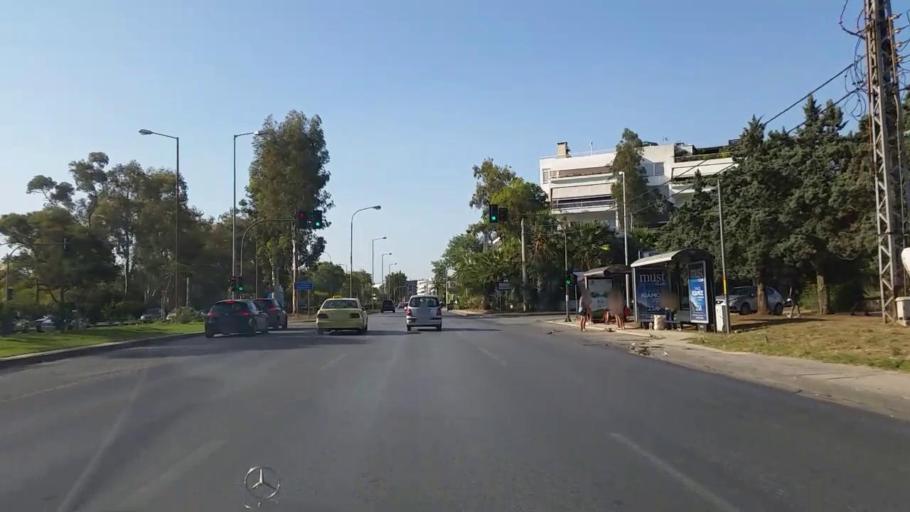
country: GR
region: Attica
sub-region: Nomarchia Athinas
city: Glyfada
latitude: 37.8542
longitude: 23.7519
